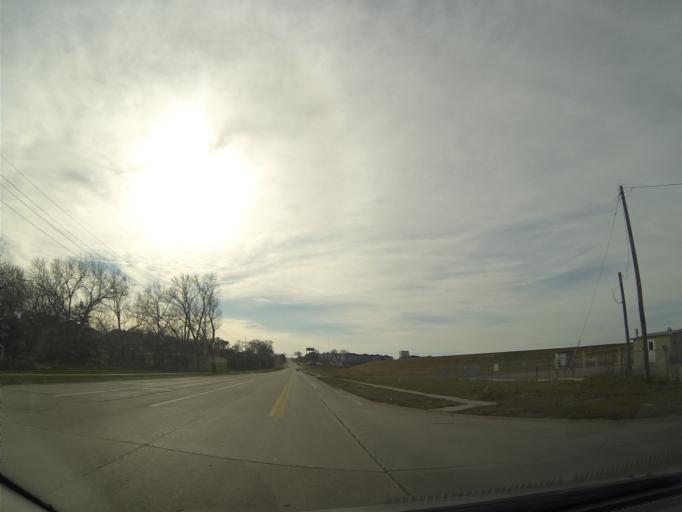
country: US
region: Nebraska
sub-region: Douglas County
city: Elkhorn
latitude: 41.2741
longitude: -96.2158
